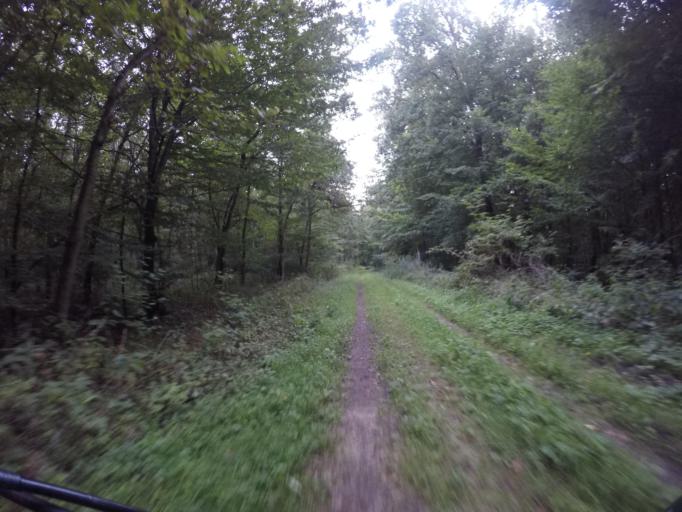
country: DE
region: Lower Saxony
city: Neu Darchau
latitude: 53.2784
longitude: 10.8904
